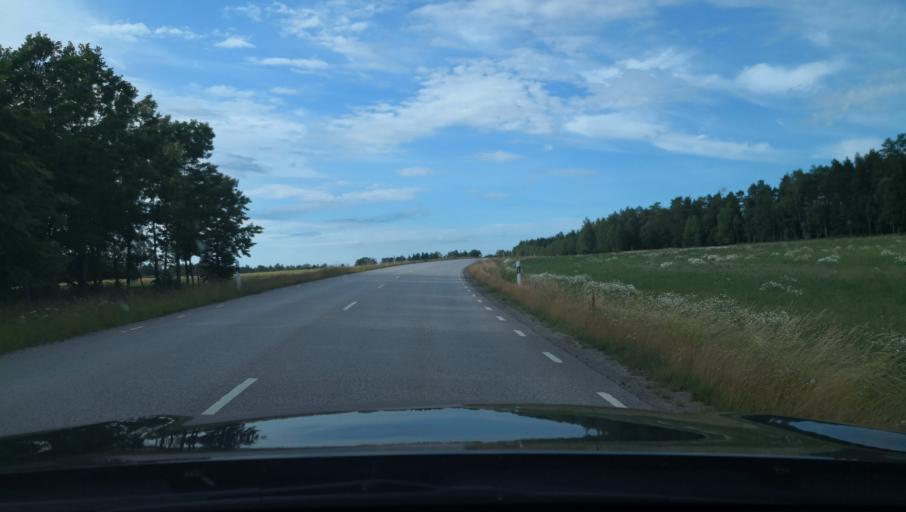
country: SE
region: Uppsala
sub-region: Habo Kommun
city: Balsta
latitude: 59.6179
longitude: 17.4982
